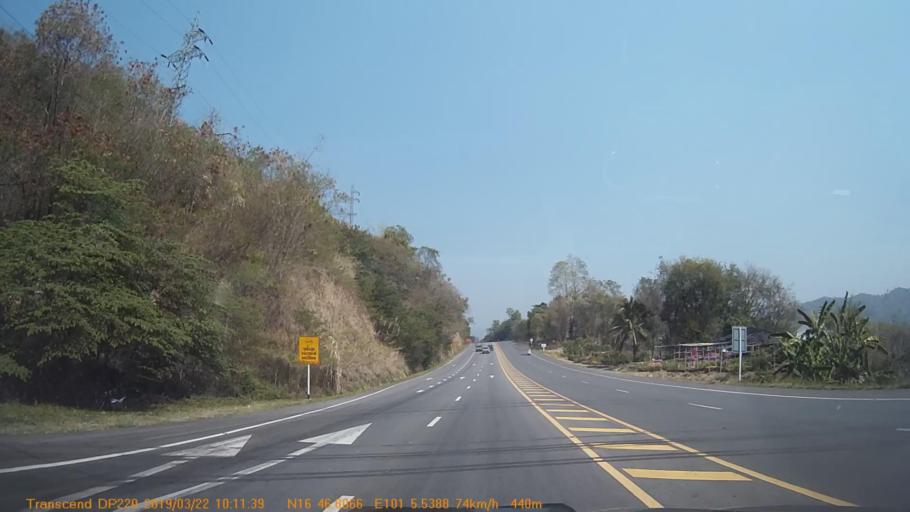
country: TH
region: Phetchabun
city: Khao Kho
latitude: 16.7805
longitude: 101.0921
